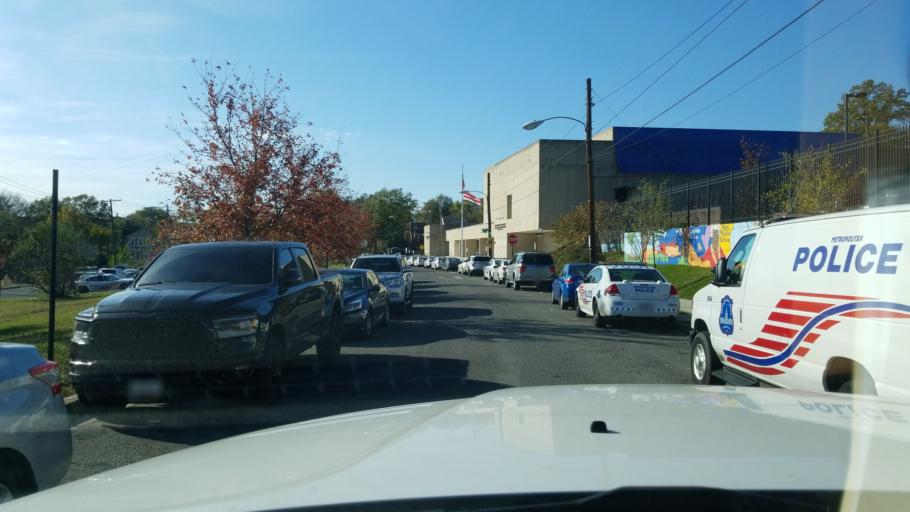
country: US
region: Maryland
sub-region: Prince George's County
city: Fairmount Heights
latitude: 38.8999
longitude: -76.9287
